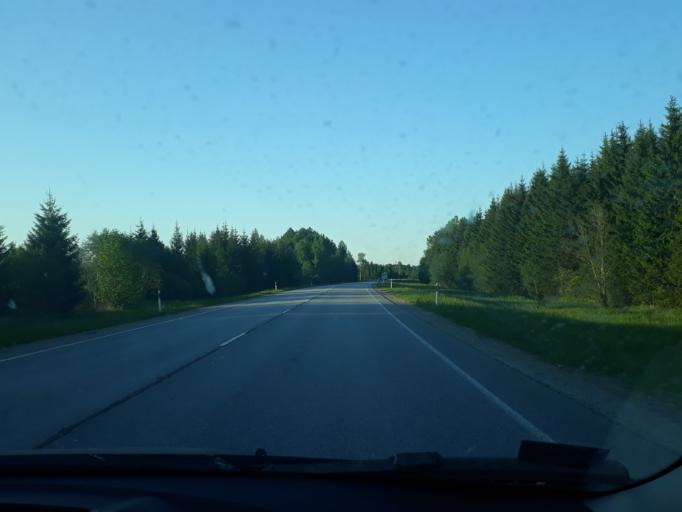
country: EE
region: Paernumaa
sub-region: Sindi linn
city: Sindi
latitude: 58.4614
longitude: 24.7005
